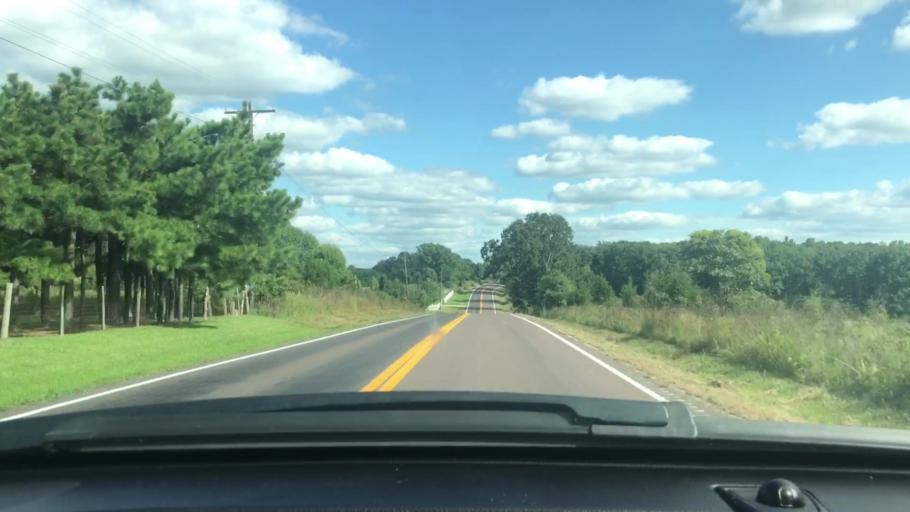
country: US
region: Missouri
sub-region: Wright County
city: Mountain Grove
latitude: 37.2326
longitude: -92.2978
